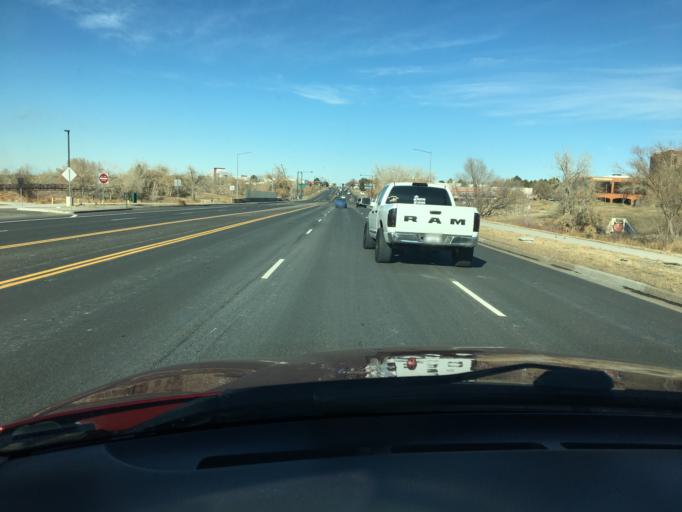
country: US
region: Colorado
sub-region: Adams County
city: Aurora
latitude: 39.6582
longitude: -104.8663
